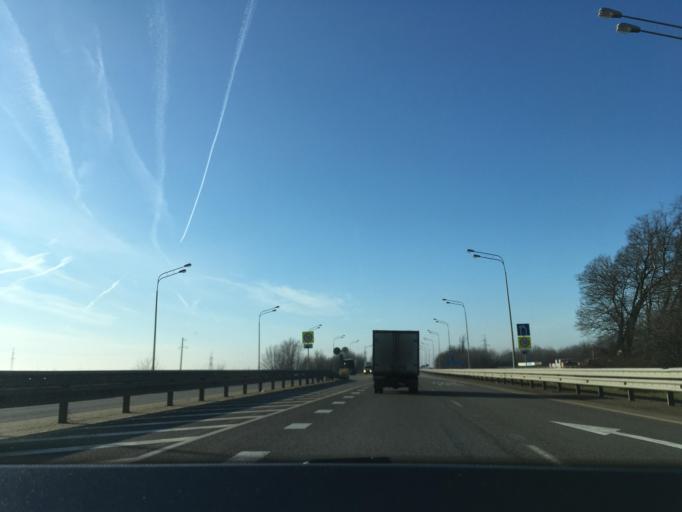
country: RU
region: Krasnodarskiy
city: Agronom
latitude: 45.1751
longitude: 39.1026
